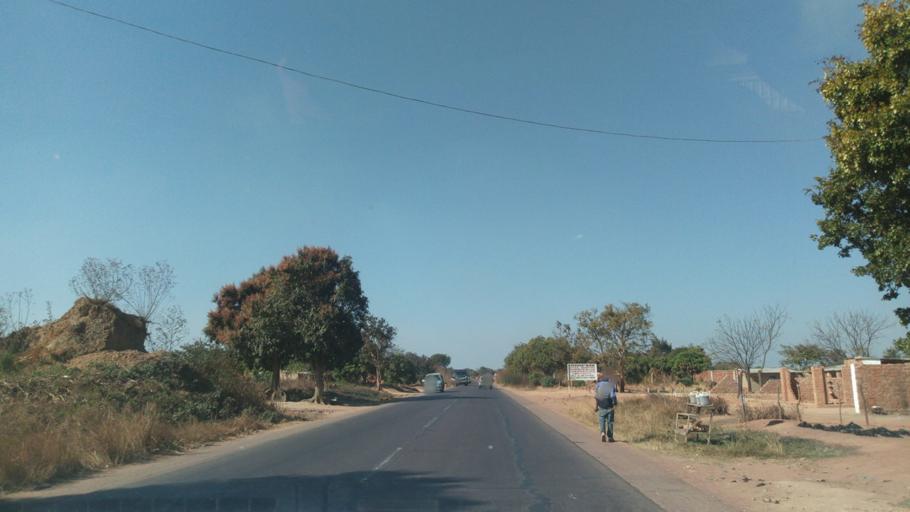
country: CD
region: Katanga
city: Lubumbashi
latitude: -11.5560
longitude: 27.5801
